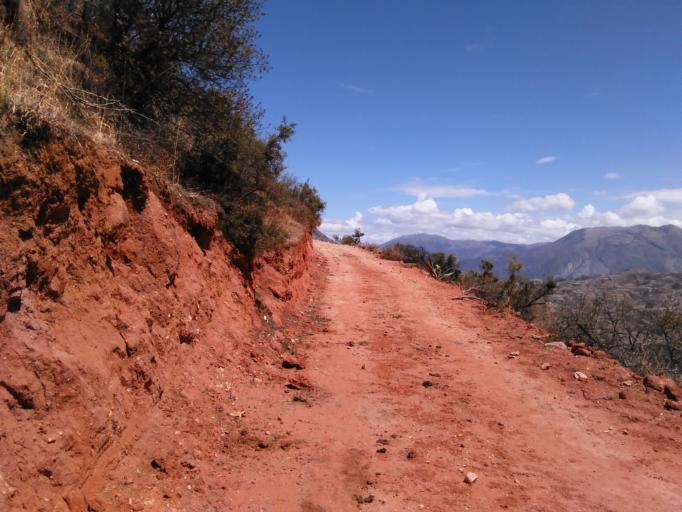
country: PE
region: Ayacucho
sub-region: Provincia de Victor Fajardo
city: Canaria
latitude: -13.8830
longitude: -73.9473
